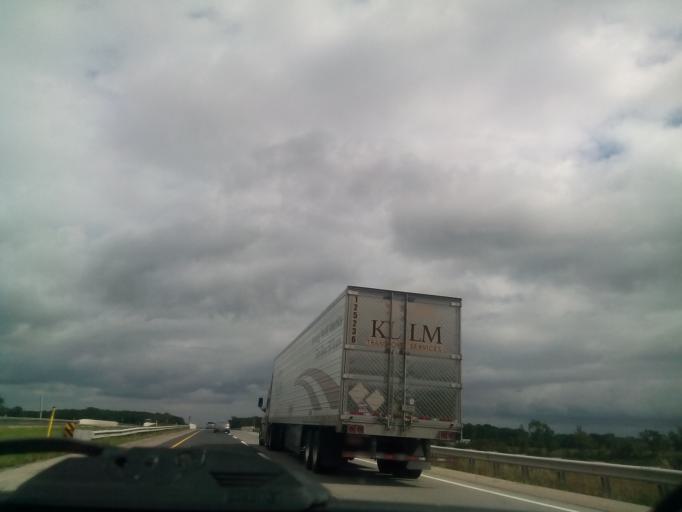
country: US
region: Indiana
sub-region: Steuben County
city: Fremont
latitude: 41.7133
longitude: -84.9470
